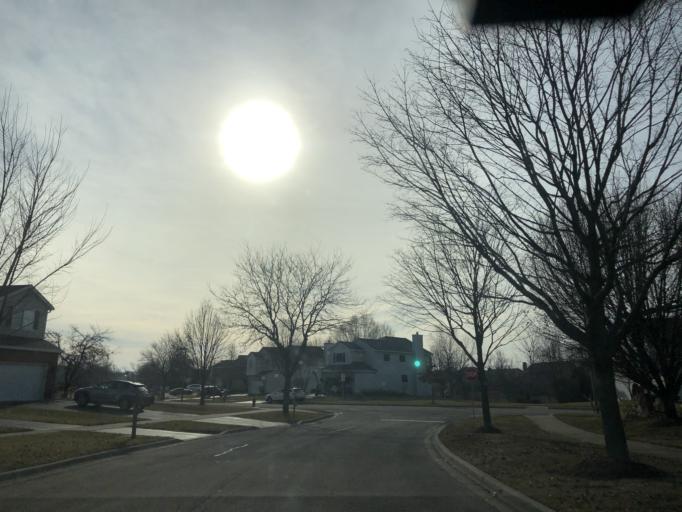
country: US
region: Illinois
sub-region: Cook County
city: Lemont
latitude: 41.7173
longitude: -88.0154
